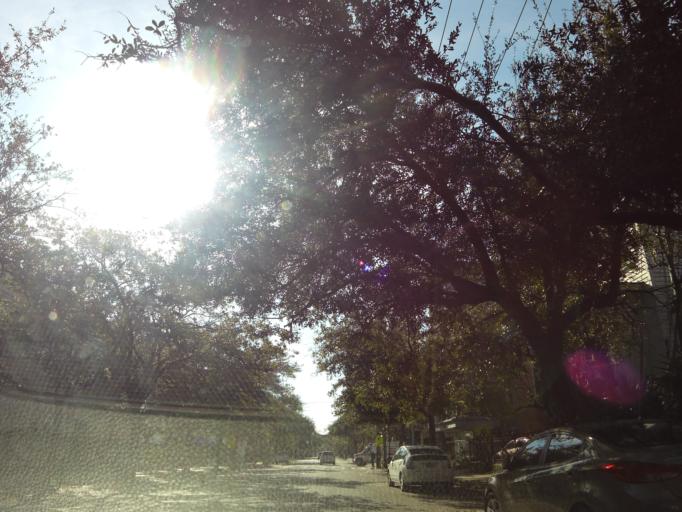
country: US
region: South Carolina
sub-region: Charleston County
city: Charleston
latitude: 32.7864
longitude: -79.9456
